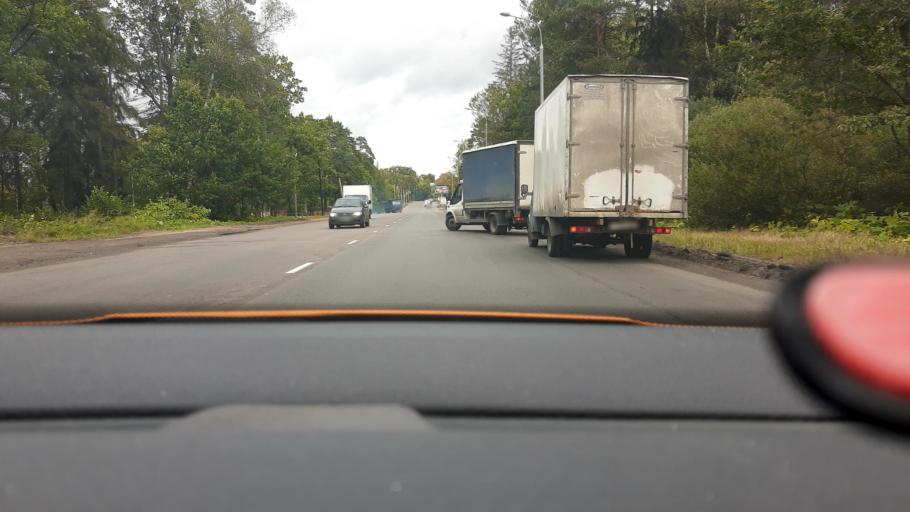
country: RU
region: Moskovskaya
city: Kostino
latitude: 56.0397
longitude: 37.9726
